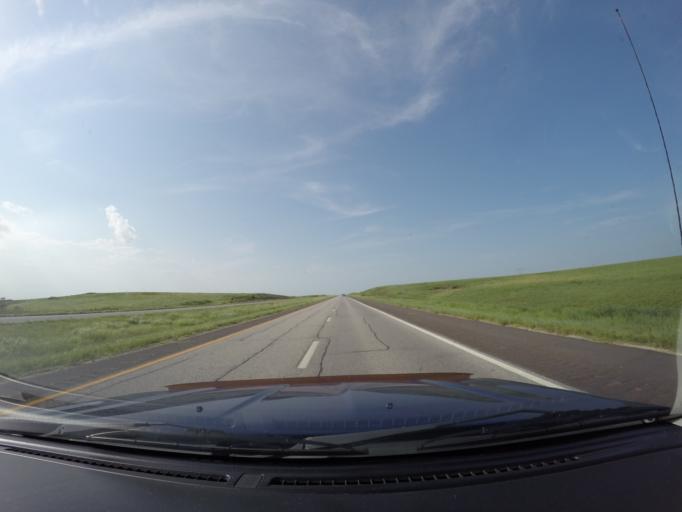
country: US
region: Kansas
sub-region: Riley County
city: Manhattan
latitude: 39.1225
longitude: -96.5381
